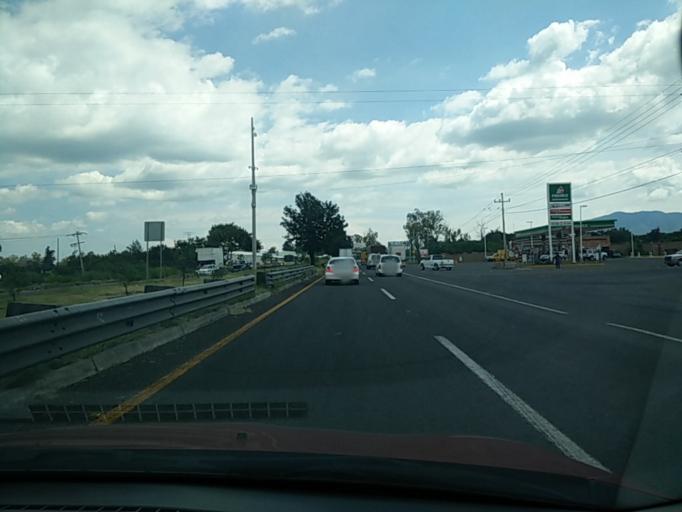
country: MX
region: Jalisco
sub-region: Tlajomulco de Zuniga
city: Rancho Alegre [Fraccionamiento]
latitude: 20.4558
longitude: -103.2513
